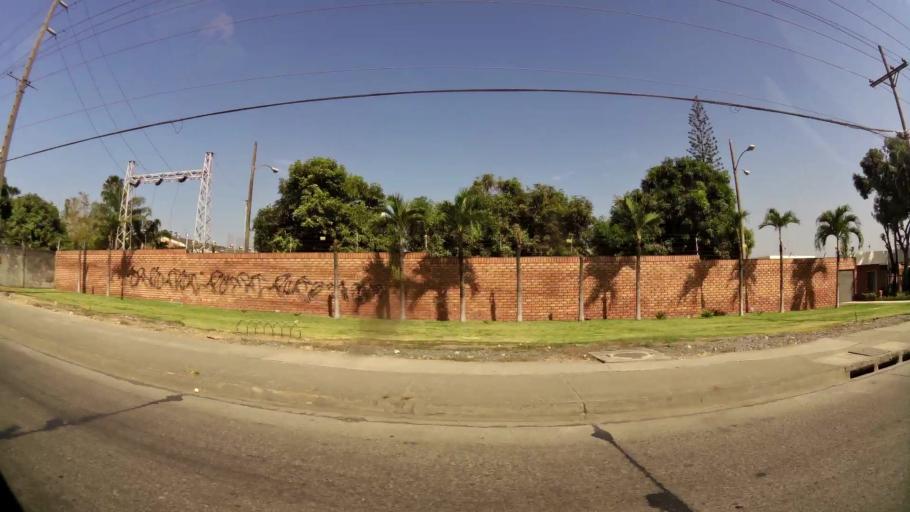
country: EC
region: Guayas
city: Santa Lucia
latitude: -2.1030
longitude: -79.9354
